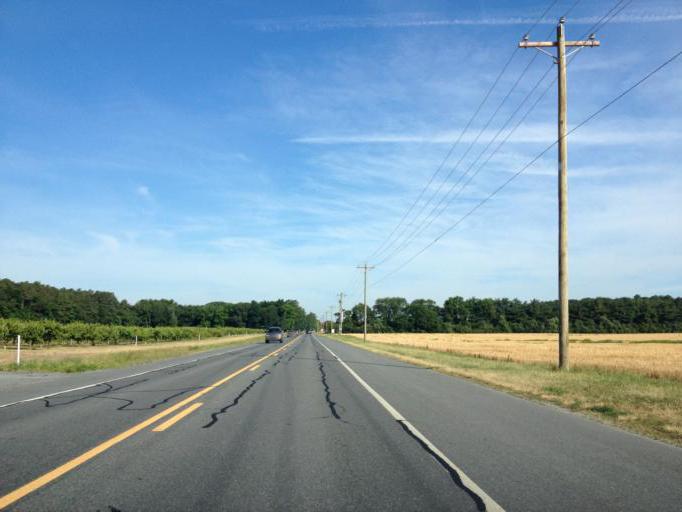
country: US
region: Delaware
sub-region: Sussex County
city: Selbyville
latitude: 38.5309
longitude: -75.2051
